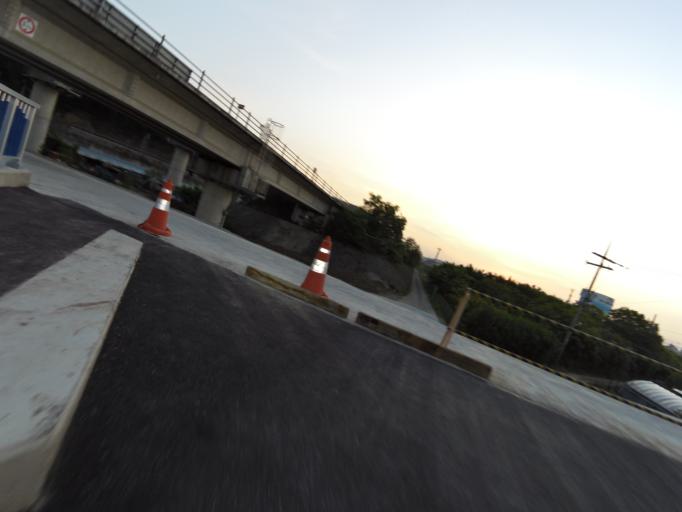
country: KR
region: Gyeongsangbuk-do
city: Gyeongsan-si
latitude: 35.8518
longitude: 128.7079
